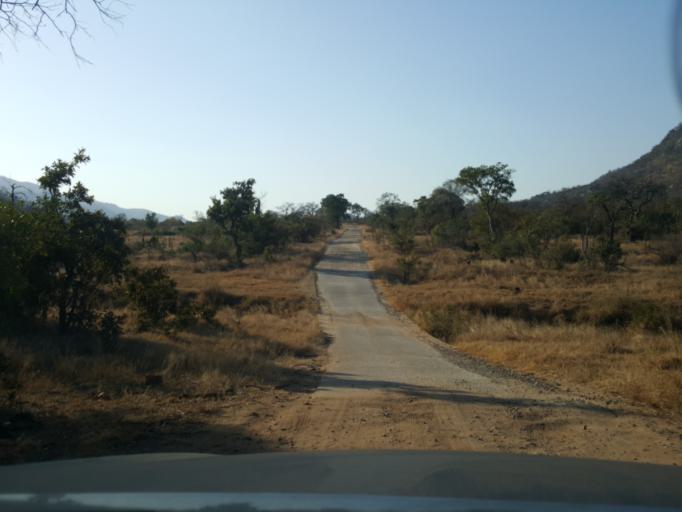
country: SZ
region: Hhohho
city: Ntfonjeni
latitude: -25.4165
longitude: 31.4414
